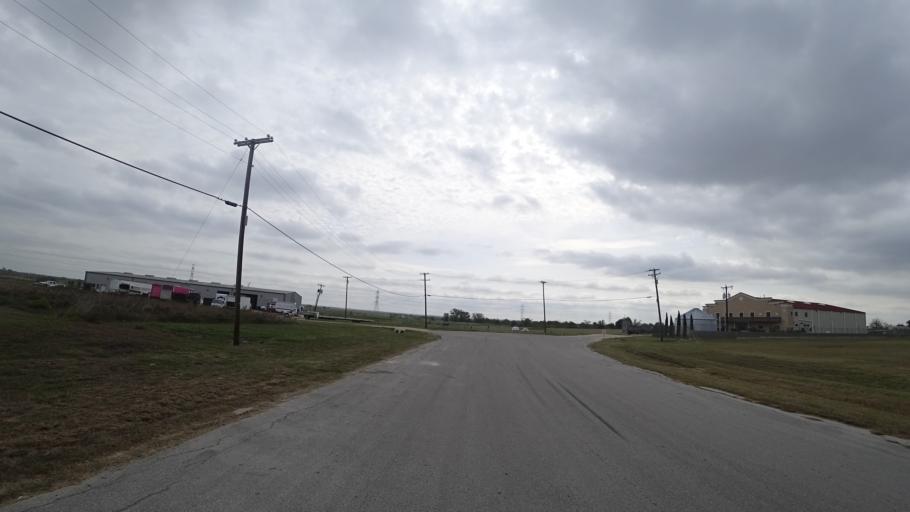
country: US
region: Texas
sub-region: Travis County
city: Manor
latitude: 30.3900
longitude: -97.5826
